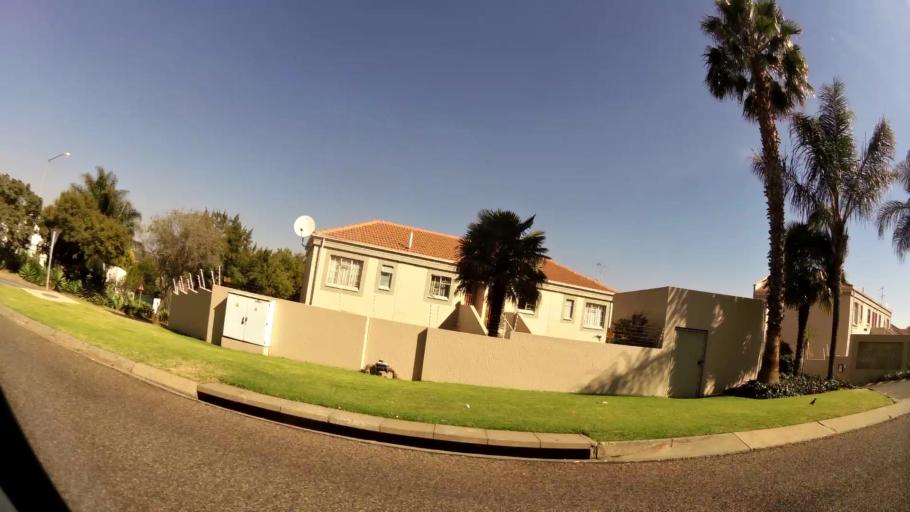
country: ZA
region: Gauteng
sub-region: City of Tshwane Metropolitan Municipality
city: Pretoria
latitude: -25.7941
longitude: 28.2293
